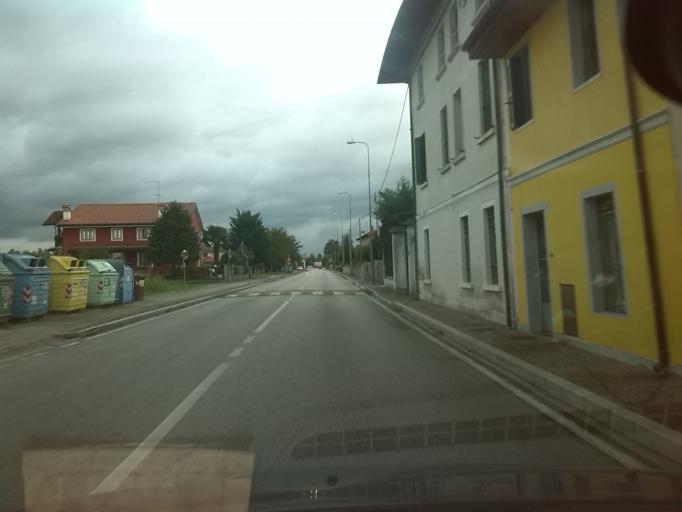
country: IT
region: Friuli Venezia Giulia
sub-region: Provincia di Udine
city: Udine
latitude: 46.0812
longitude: 13.2747
